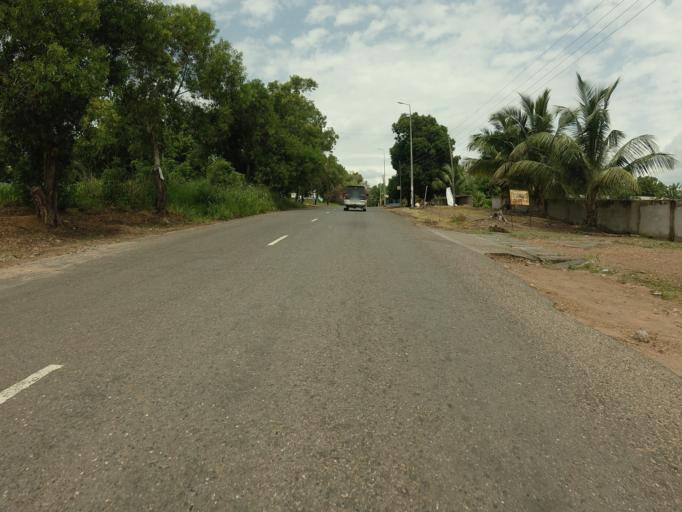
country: GH
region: Volta
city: Ho
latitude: 6.5966
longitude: 0.4630
